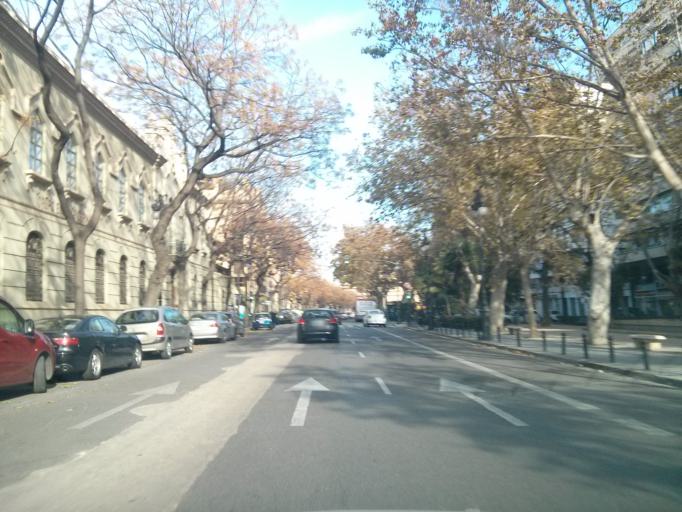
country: ES
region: Valencia
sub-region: Provincia de Valencia
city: Valencia
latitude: 39.4769
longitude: -0.3840
